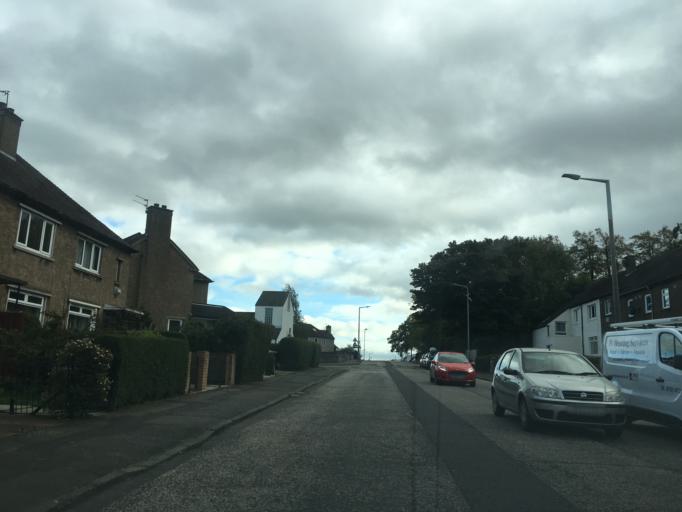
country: GB
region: Scotland
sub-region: Edinburgh
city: Edinburgh
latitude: 55.9659
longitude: -3.2500
